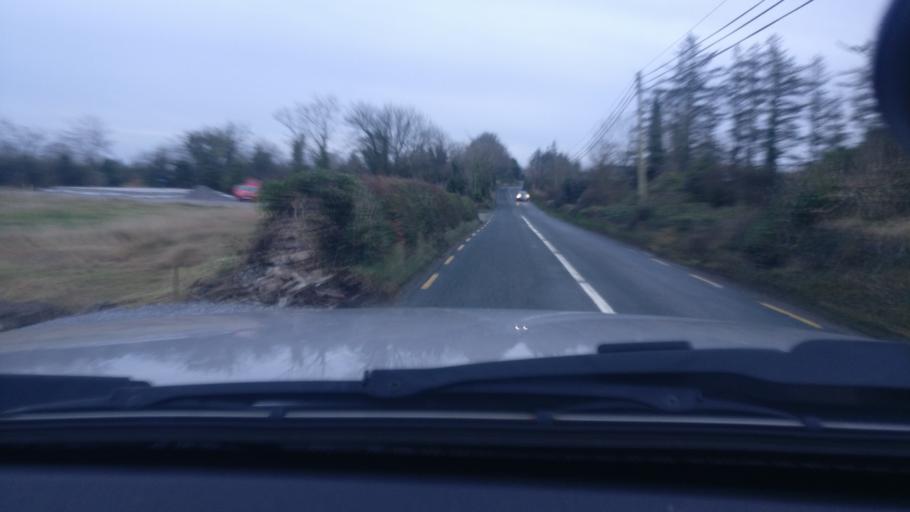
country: IE
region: Connaught
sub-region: County Galway
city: Loughrea
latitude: 53.1704
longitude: -8.5237
